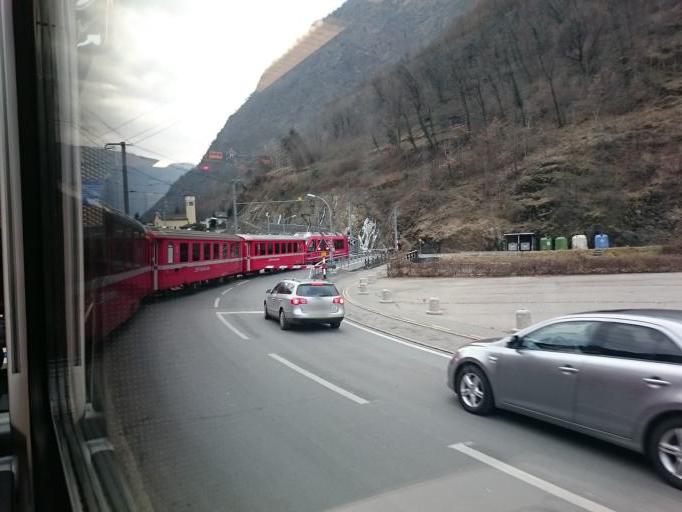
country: CH
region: Grisons
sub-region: Bernina District
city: Brusio
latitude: 46.2359
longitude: 10.1400
